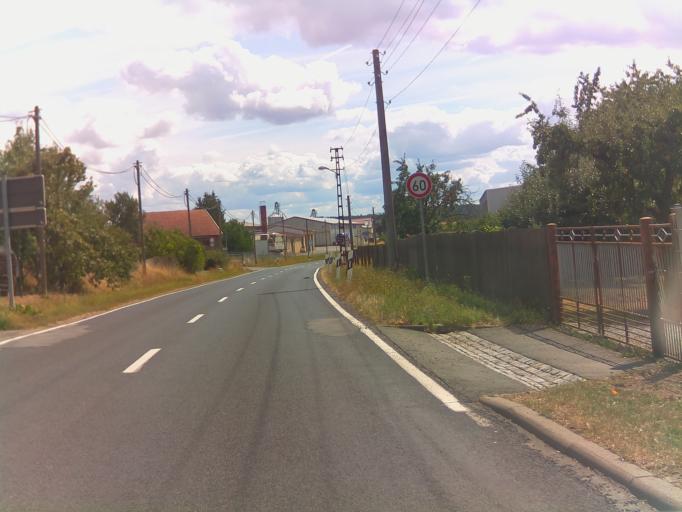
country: DE
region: Thuringia
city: Wolfershausen
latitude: 50.4483
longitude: 10.4573
